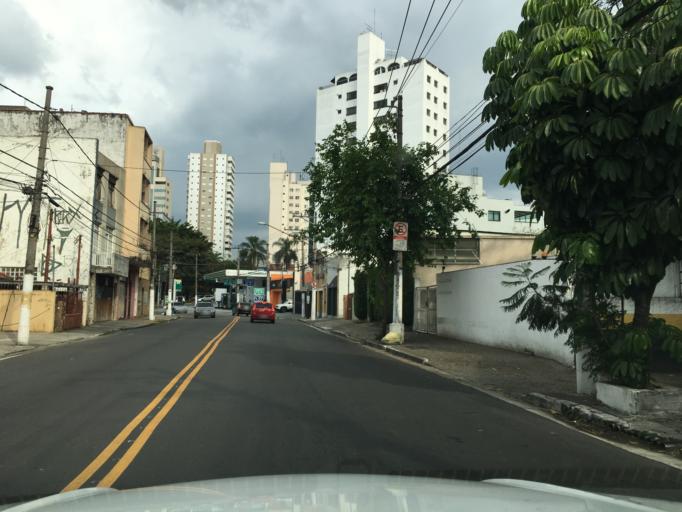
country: BR
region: Sao Paulo
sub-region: Sao Paulo
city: Sao Paulo
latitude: -23.4962
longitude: -46.6296
